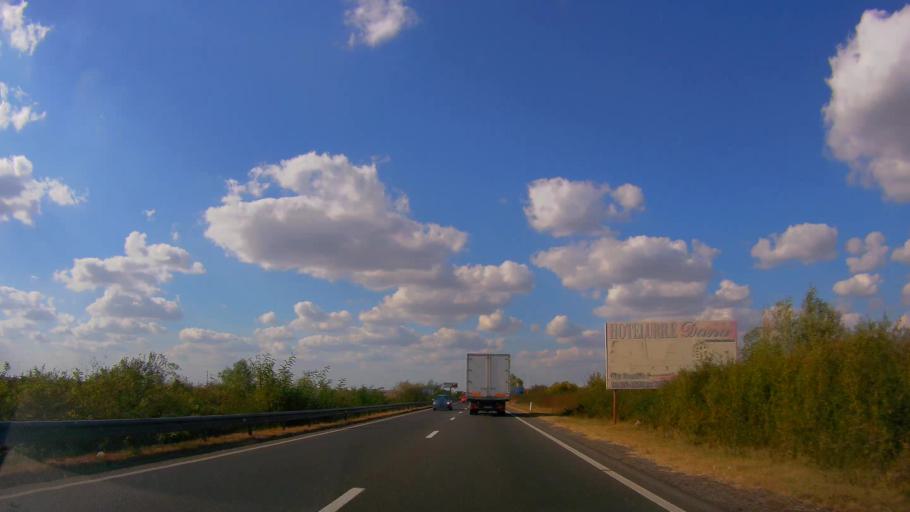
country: RO
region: Satu Mare
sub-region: Oras Ardud
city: Madaras
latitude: 47.7253
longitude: 22.8864
